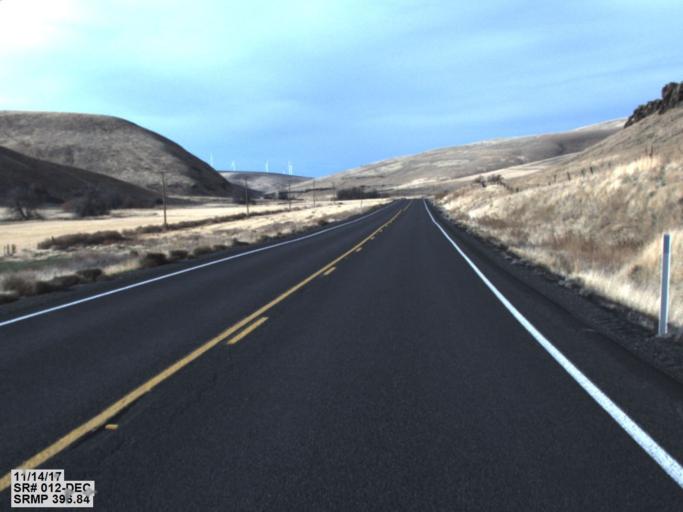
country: US
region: Washington
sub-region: Garfield County
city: Pomeroy
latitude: 46.4747
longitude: -117.7266
